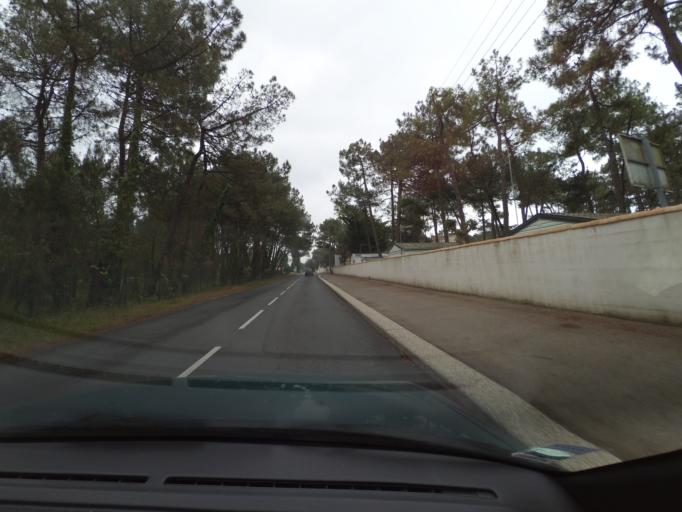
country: FR
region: Pays de la Loire
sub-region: Departement de la Vendee
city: Angles
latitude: 46.3464
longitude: -1.3514
